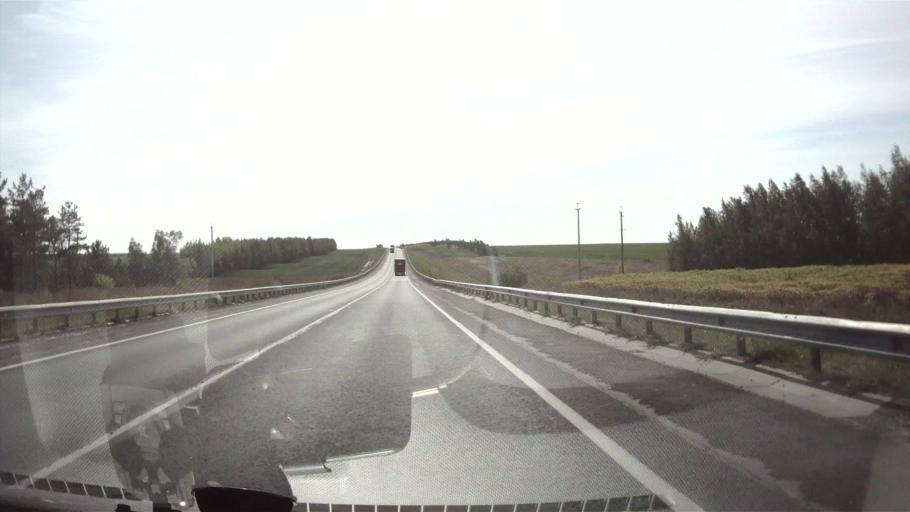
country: RU
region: Samara
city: Syzran'
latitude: 52.9021
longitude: 48.2969
